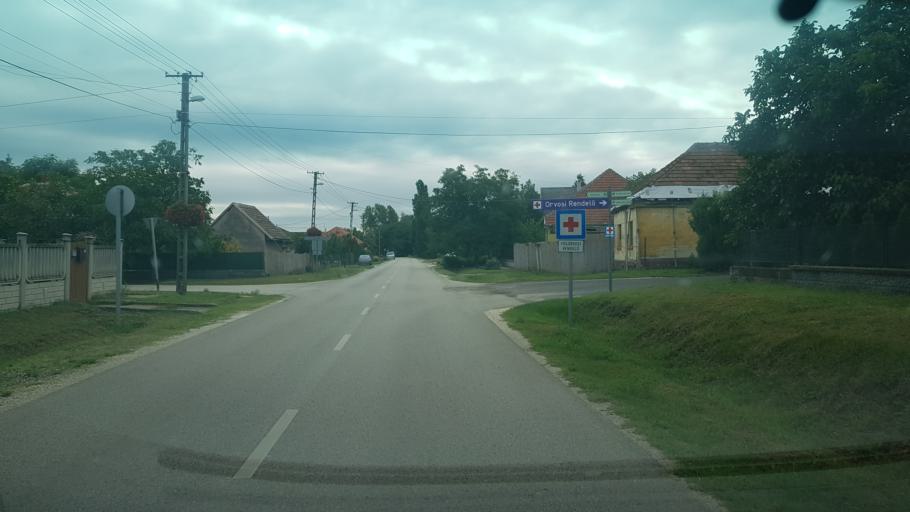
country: HU
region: Pest
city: Dunavarsany
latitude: 47.2868
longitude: 19.0337
